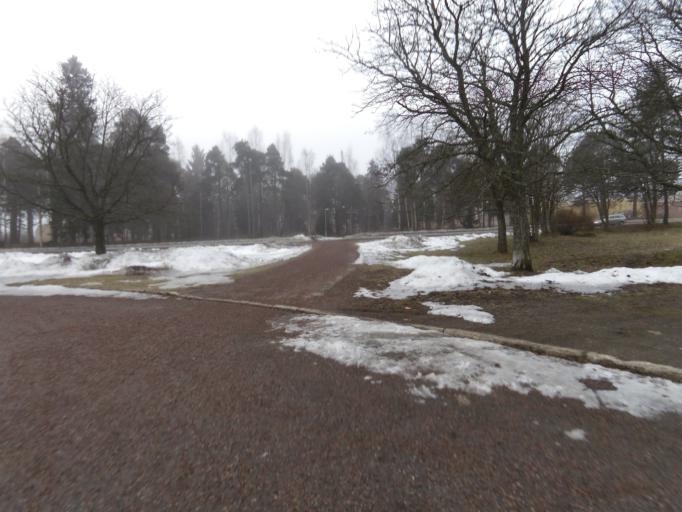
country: SE
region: Gaevleborg
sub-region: Gavle Kommun
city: Gavle
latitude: 60.6620
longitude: 17.1464
